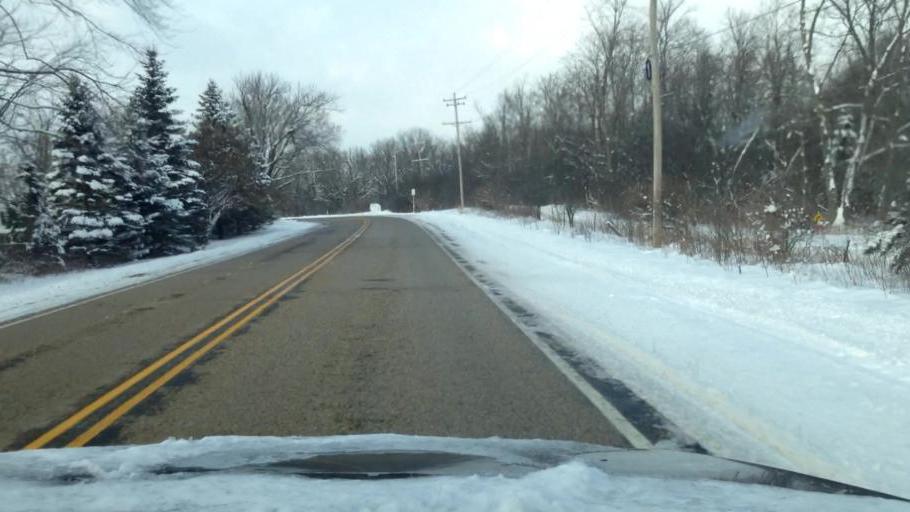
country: US
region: Wisconsin
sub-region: Walworth County
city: East Troy
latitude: 42.8396
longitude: -88.4242
